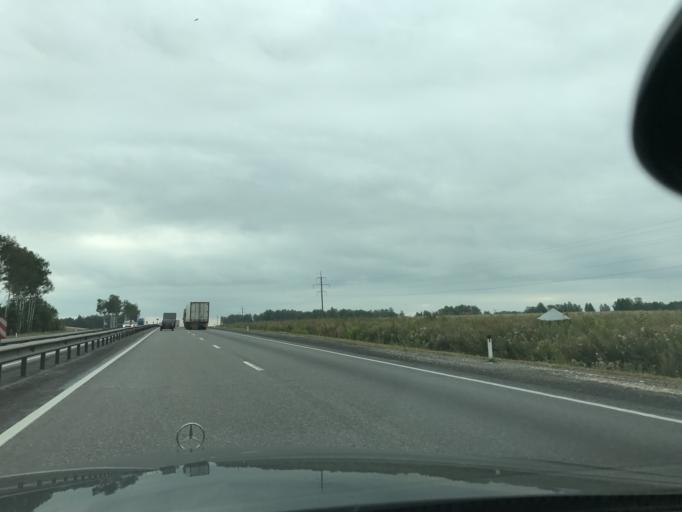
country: RU
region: Vladimir
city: Gorokhovets
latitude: 56.1606
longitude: 42.5875
